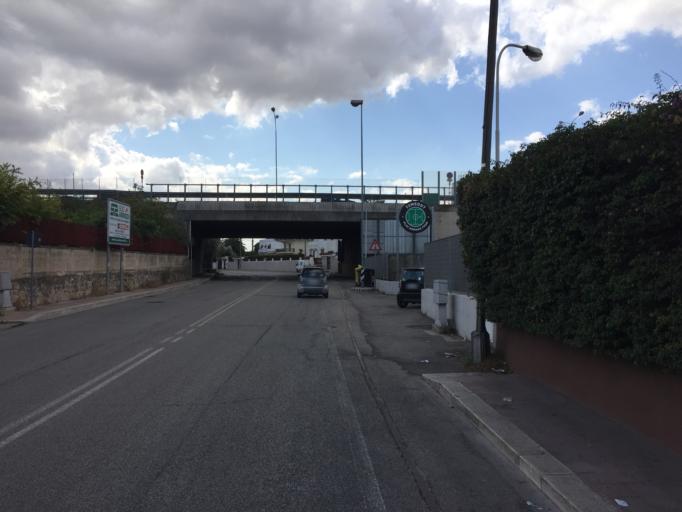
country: IT
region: Apulia
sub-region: Provincia di Bari
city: Bari
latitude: 41.0900
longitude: 16.8837
